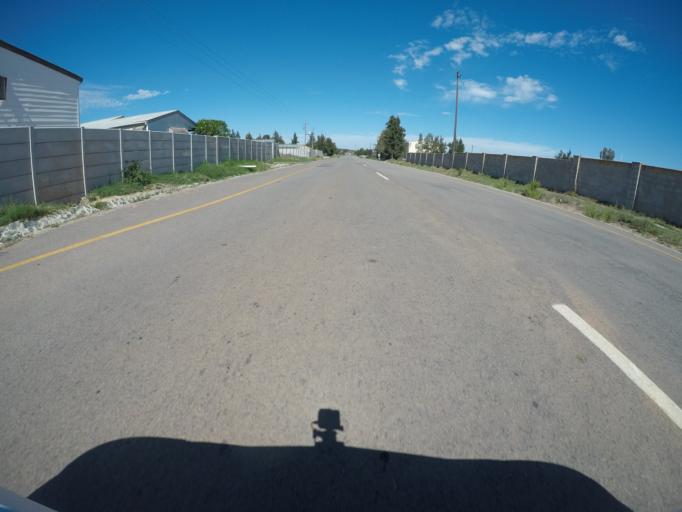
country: ZA
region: Western Cape
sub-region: West Coast District Municipality
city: Malmesbury
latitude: -33.5760
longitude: 18.6469
